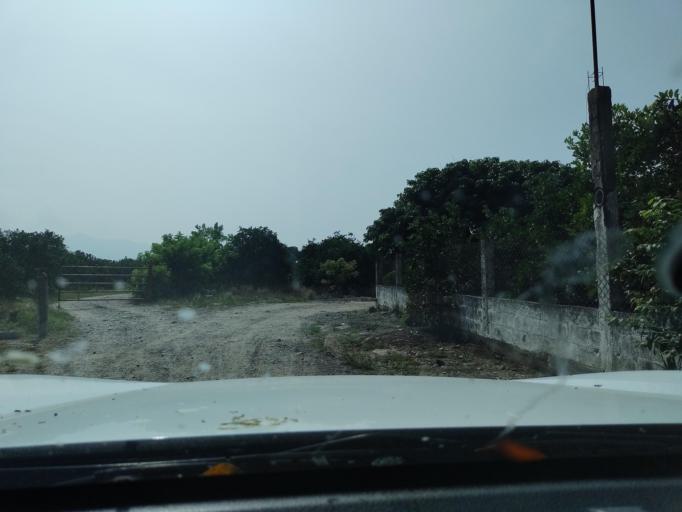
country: MX
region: Veracruz
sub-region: Martinez de la Torre
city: El Progreso
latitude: 20.0781
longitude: -97.0039
